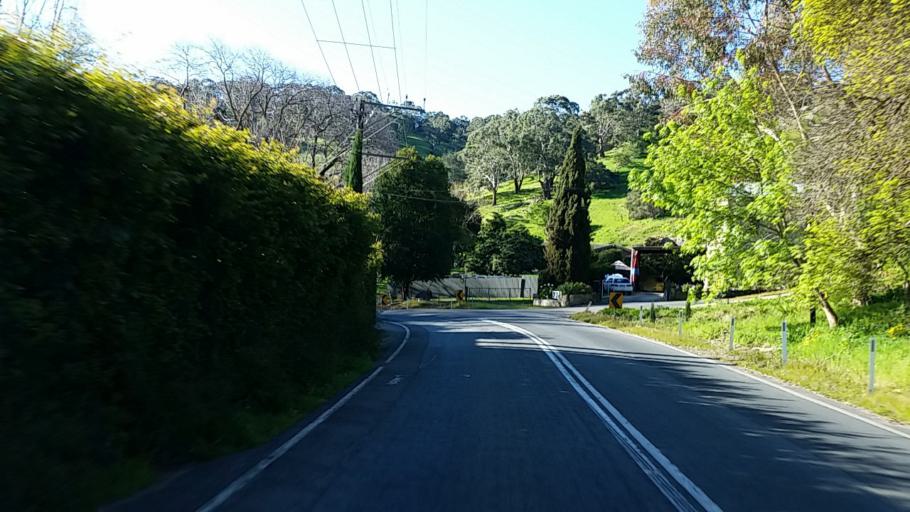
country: AU
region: South Australia
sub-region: Adelaide Hills
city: Adelaide Hills
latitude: -34.9229
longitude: 138.7184
